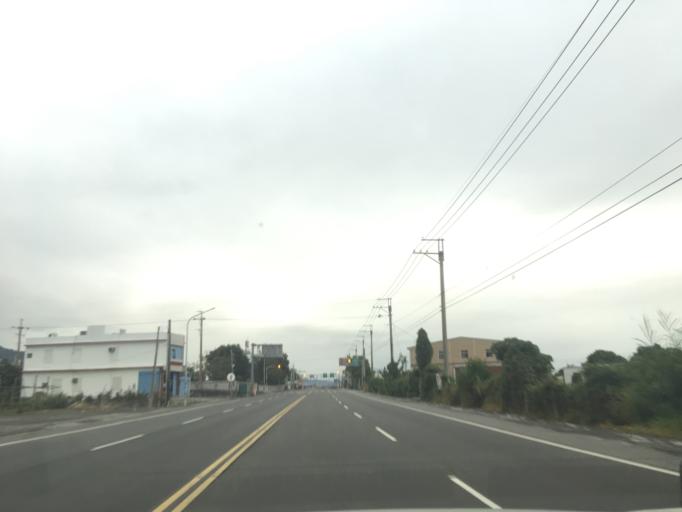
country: TW
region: Taiwan
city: Taitung City
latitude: 22.6866
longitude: 121.0444
